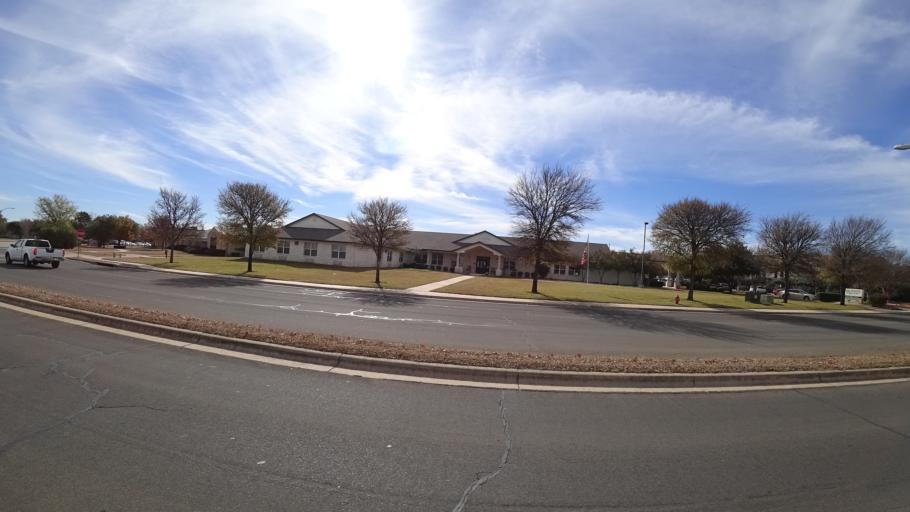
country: US
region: Texas
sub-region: Williamson County
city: Cedar Park
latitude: 30.5198
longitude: -97.8246
